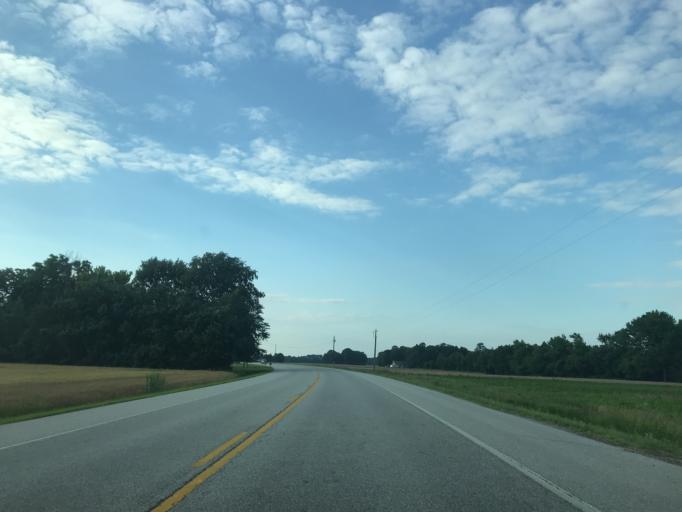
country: US
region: Maryland
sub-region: Caroline County
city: Federalsburg
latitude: 38.7710
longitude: -75.7871
